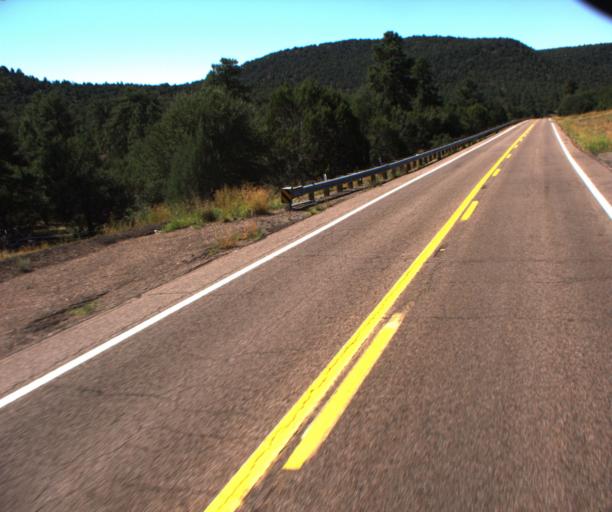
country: US
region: Arizona
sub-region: Navajo County
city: Cibecue
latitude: 33.9043
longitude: -110.3643
